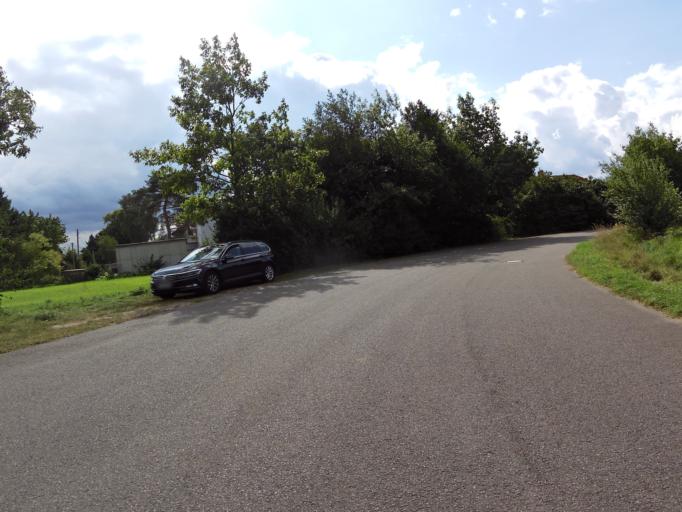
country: DE
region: Saxony
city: Rackwitz
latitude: 51.3919
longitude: 12.3587
